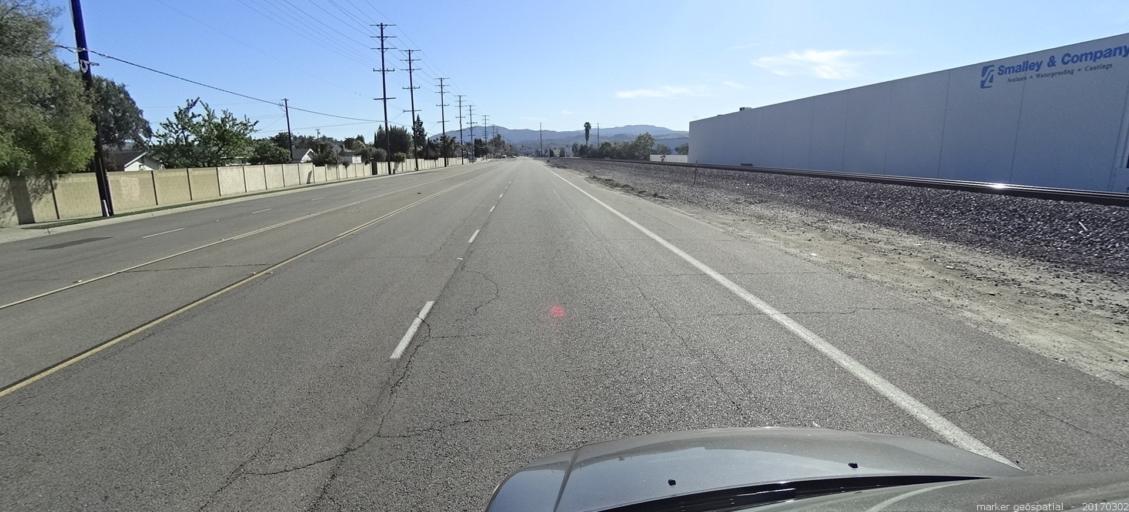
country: US
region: California
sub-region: Orange County
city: Yorba Linda
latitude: 33.8656
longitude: -117.8096
